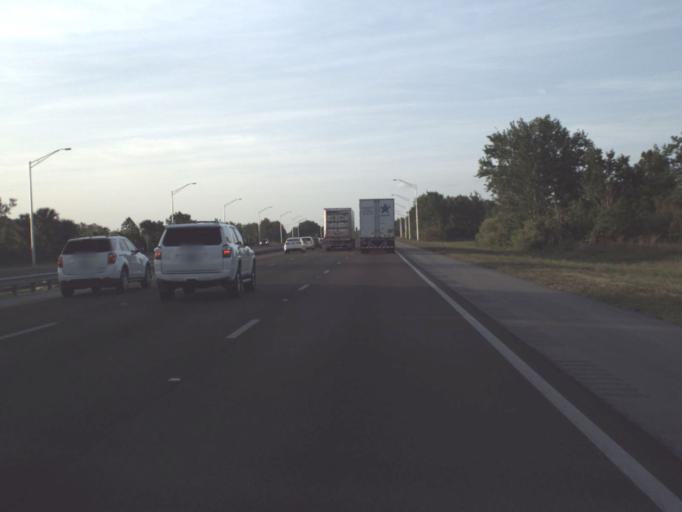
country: US
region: Florida
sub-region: Volusia County
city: Oak Hill
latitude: 28.7634
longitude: -80.8915
